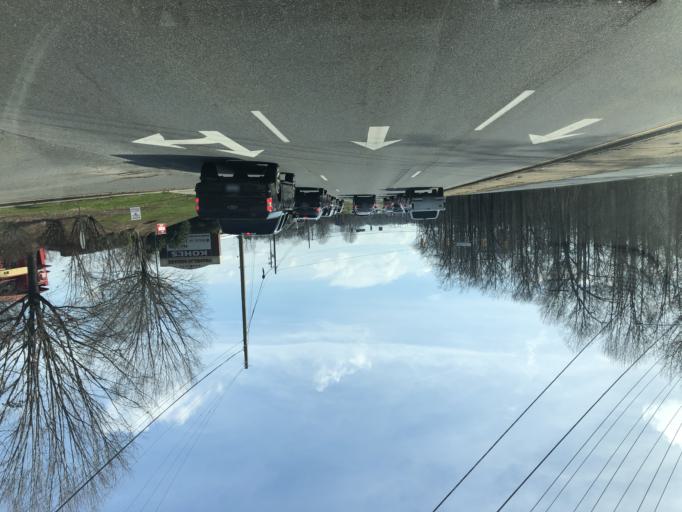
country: US
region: North Carolina
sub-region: Gaston County
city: Lowell
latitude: 35.2577
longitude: -81.1153
